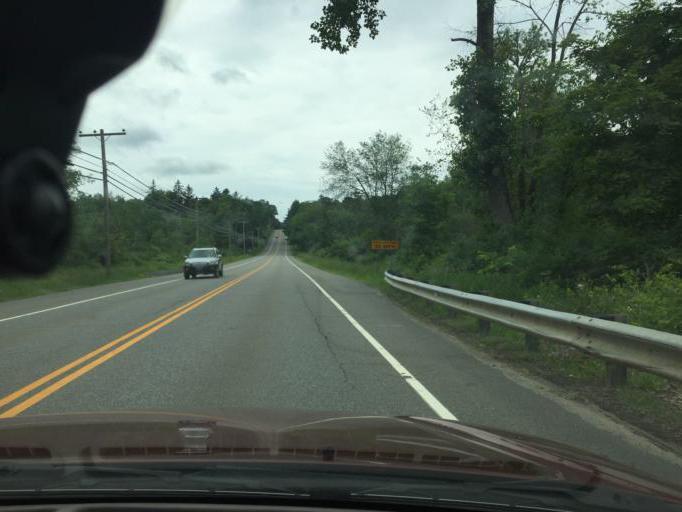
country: US
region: Connecticut
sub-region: Litchfield County
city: Litchfield
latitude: 41.7560
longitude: -73.1829
